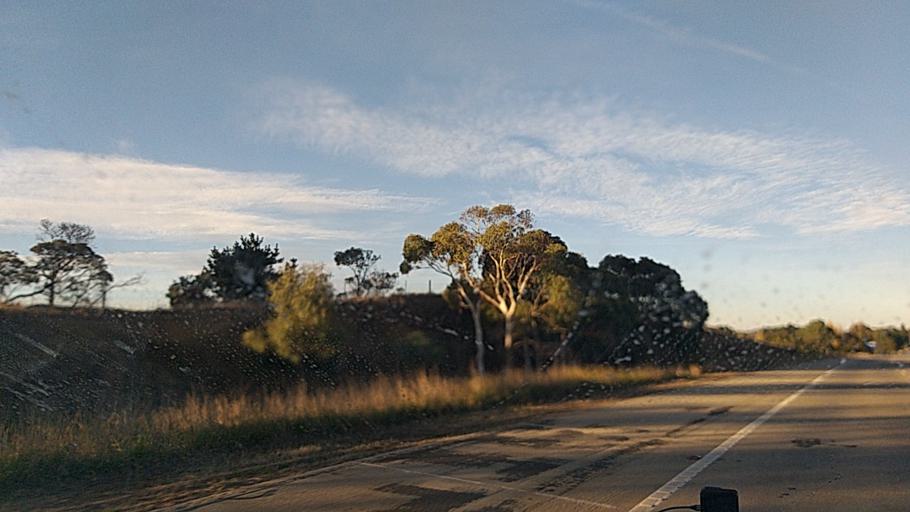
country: AU
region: New South Wales
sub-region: Yass Valley
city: Gundaroo
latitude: -35.1369
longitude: 149.3389
